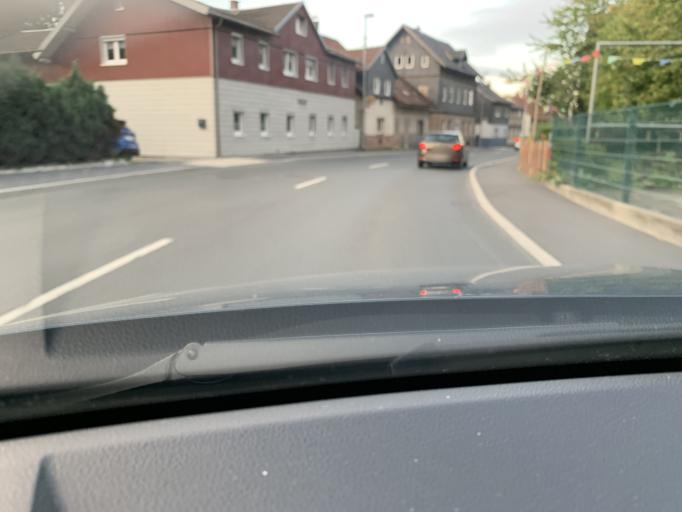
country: DE
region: Bavaria
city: Foritz
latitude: 50.3588
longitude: 11.2102
